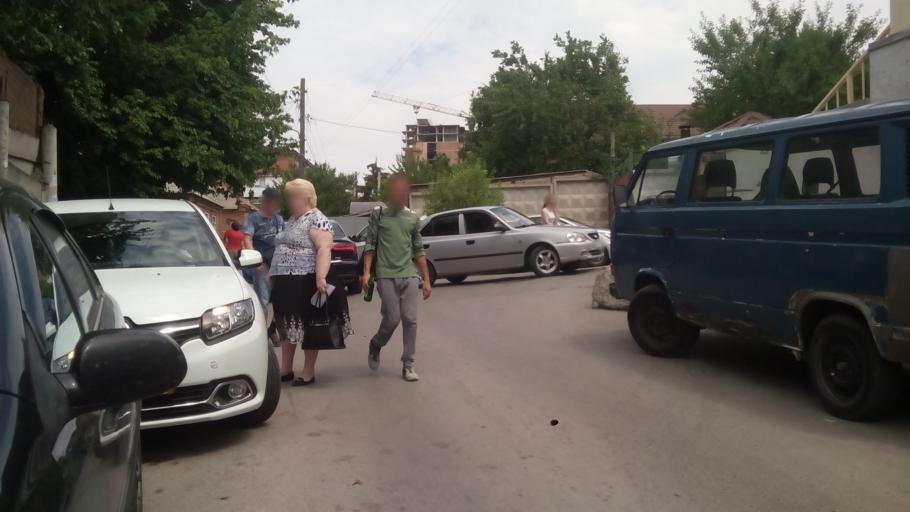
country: RU
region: Rostov
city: Rostov-na-Donu
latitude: 47.2471
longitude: 39.7422
